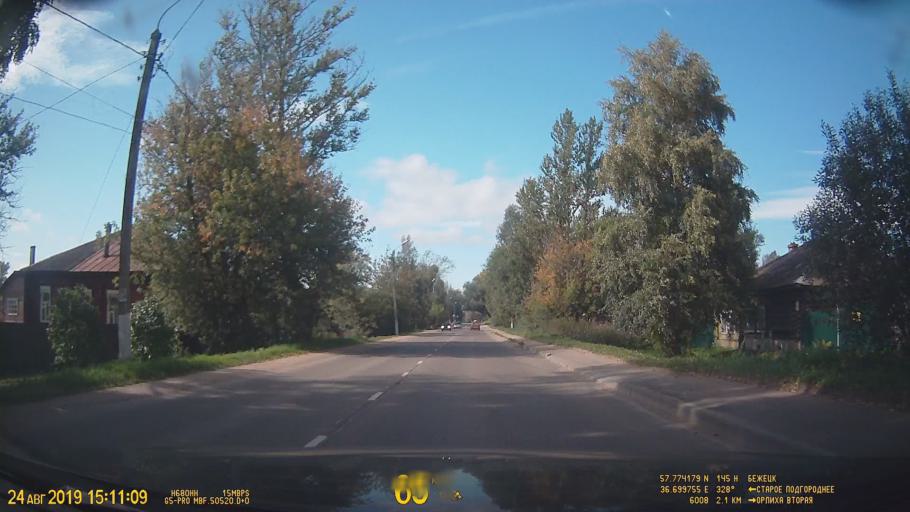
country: RU
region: Tverskaya
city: Bezhetsk
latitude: 57.7743
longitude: 36.6997
